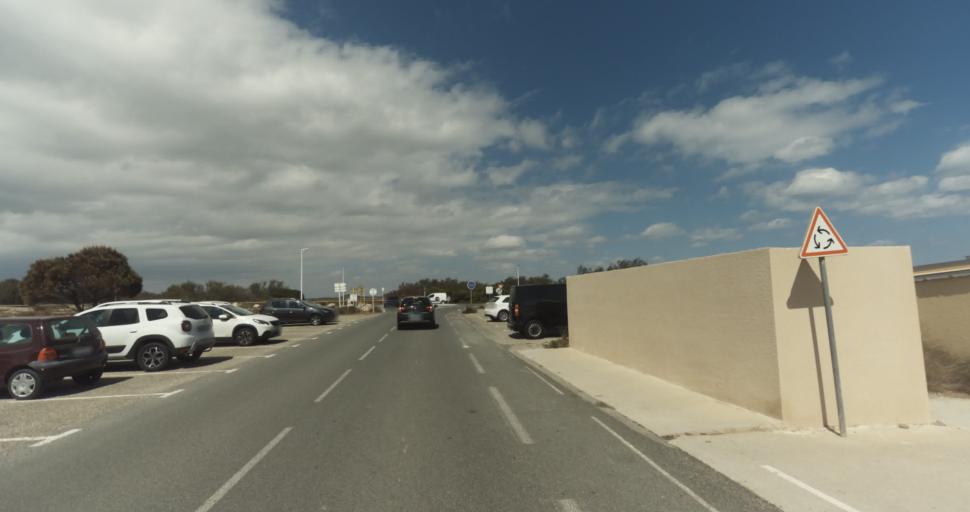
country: FR
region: Languedoc-Roussillon
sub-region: Departement de l'Aude
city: Leucate
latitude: 42.8788
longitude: 3.0437
